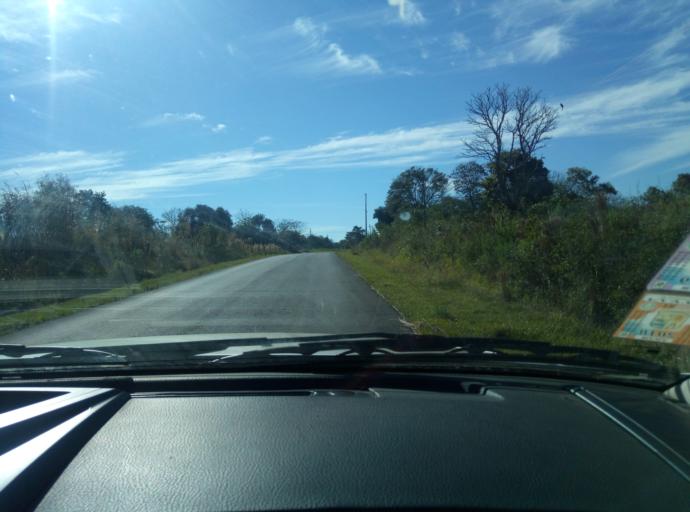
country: PY
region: Caaguazu
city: Carayao
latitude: -25.1694
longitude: -56.3130
